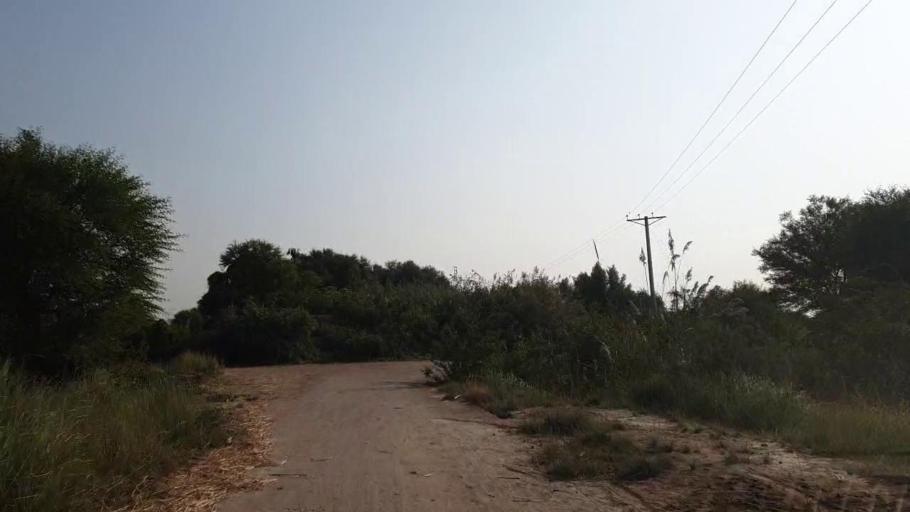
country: PK
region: Sindh
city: Bulri
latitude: 24.9797
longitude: 68.3779
